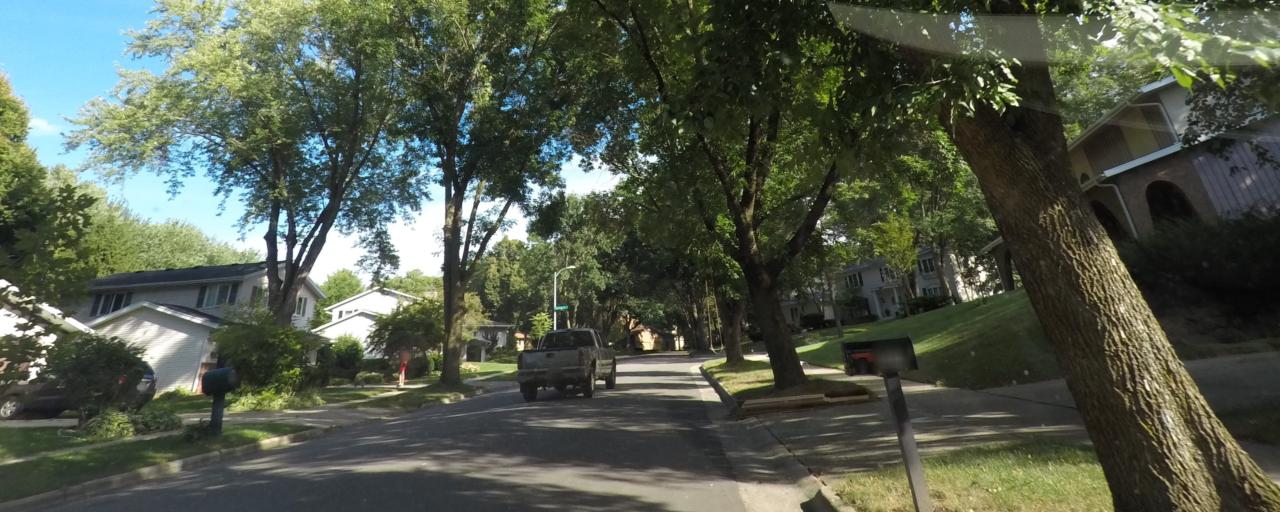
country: US
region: Wisconsin
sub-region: Dane County
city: Middleton
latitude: 43.0742
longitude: -89.5049
